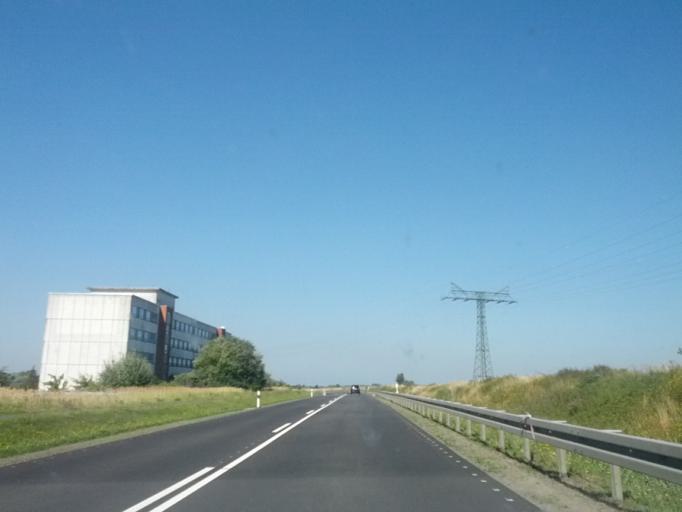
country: DE
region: Mecklenburg-Vorpommern
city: Sagard
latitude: 54.5030
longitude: 13.5566
